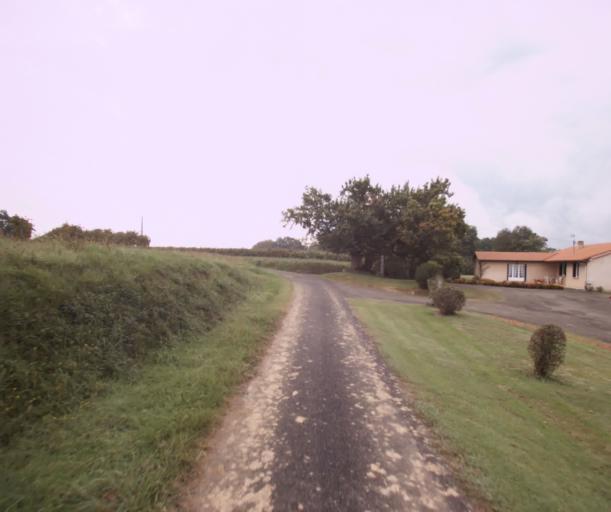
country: FR
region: Midi-Pyrenees
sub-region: Departement du Gers
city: Cazaubon
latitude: 43.9235
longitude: -0.1347
